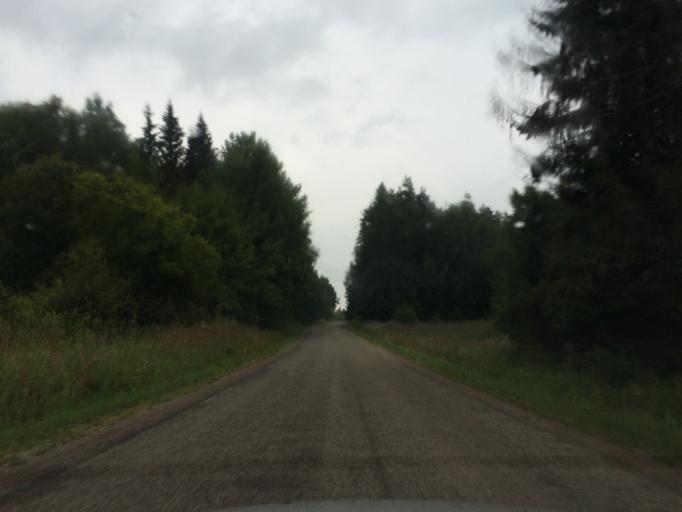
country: LV
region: Rezekne
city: Rezekne
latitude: 56.5687
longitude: 27.4634
